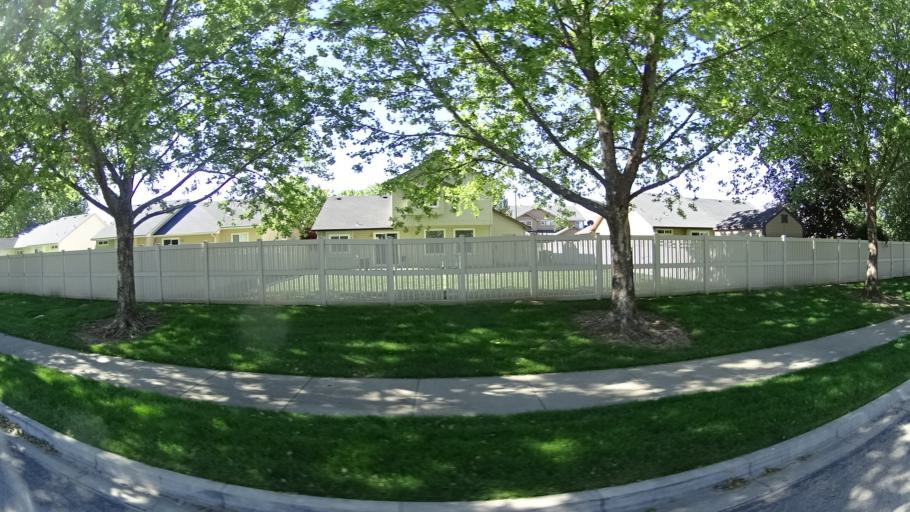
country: US
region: Idaho
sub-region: Ada County
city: Meridian
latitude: 43.6551
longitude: -116.4319
